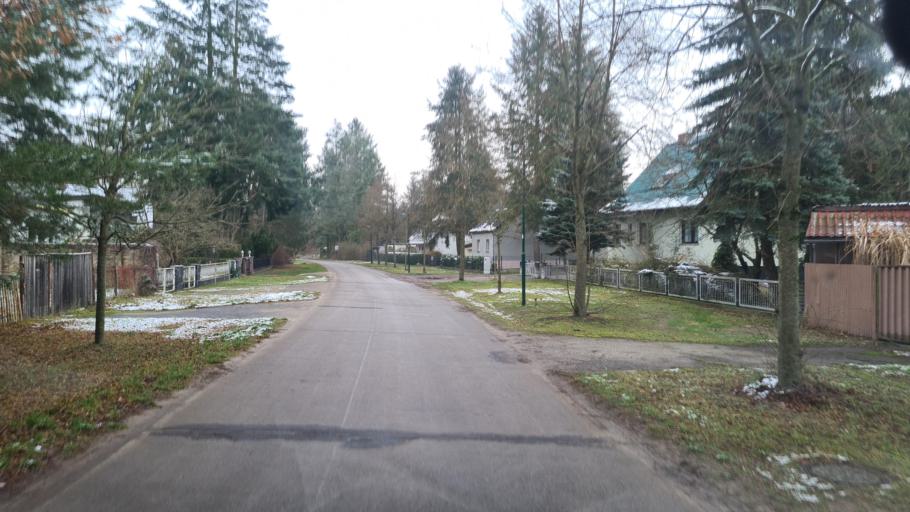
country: DE
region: Brandenburg
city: Rehfelde
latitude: 52.4565
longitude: 13.9099
